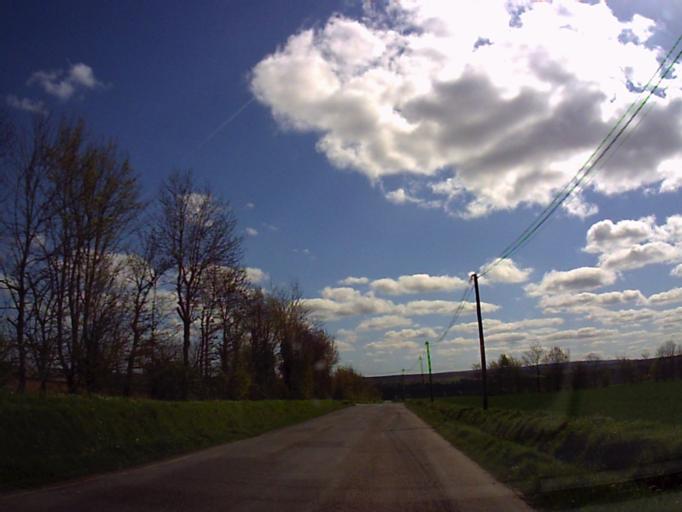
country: FR
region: Brittany
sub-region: Departement d'Ille-et-Vilaine
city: Saint-Meen-le-Grand
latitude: 48.1417
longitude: -2.1566
